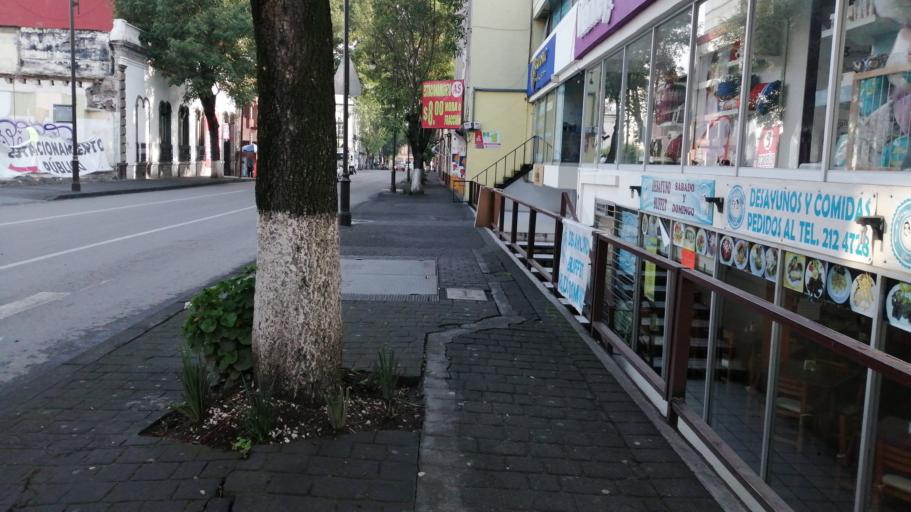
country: MX
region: Mexico
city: Toluca
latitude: 19.2884
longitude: -99.6500
